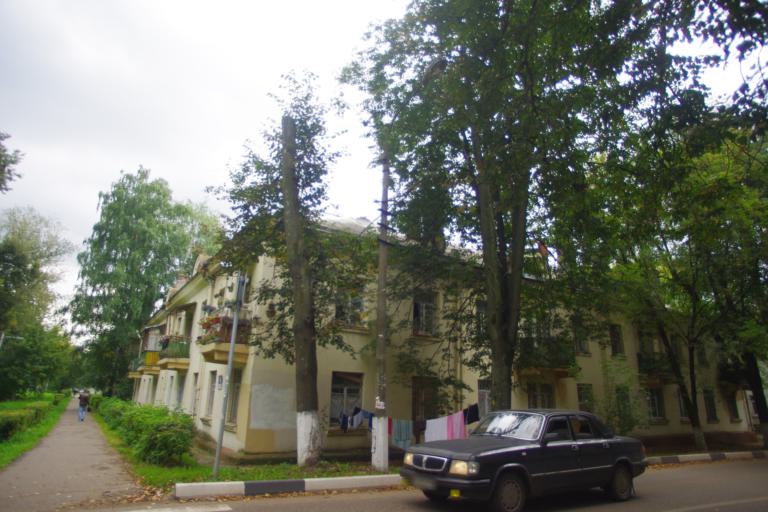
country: RU
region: Moskovskaya
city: Krasnogorsk
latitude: 55.8185
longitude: 37.3371
